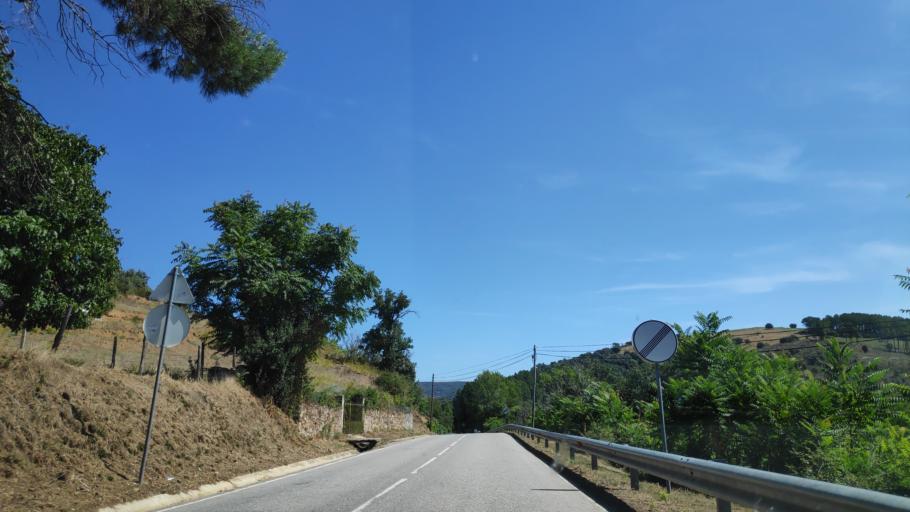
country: PT
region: Braganca
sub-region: Braganca Municipality
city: Braganca
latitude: 41.8736
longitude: -6.7475
